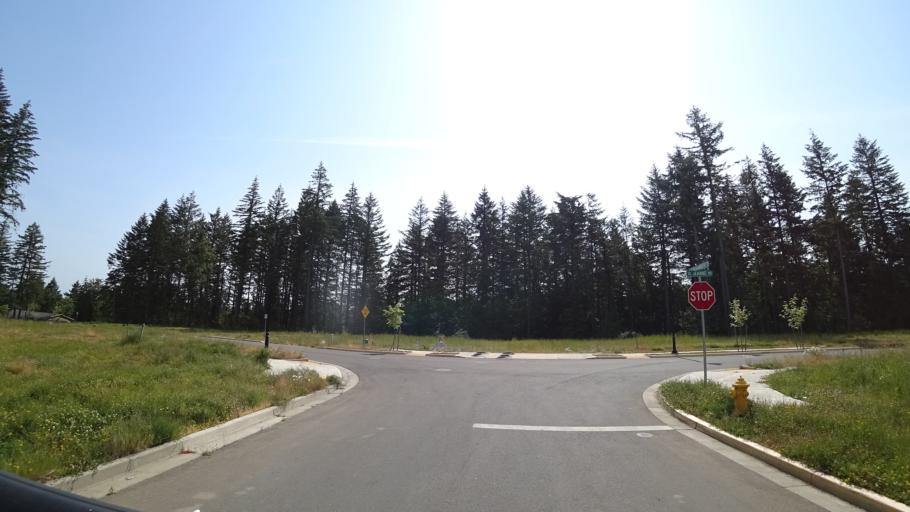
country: US
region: Oregon
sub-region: Clackamas County
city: Happy Valley
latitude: 45.4519
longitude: -122.5038
